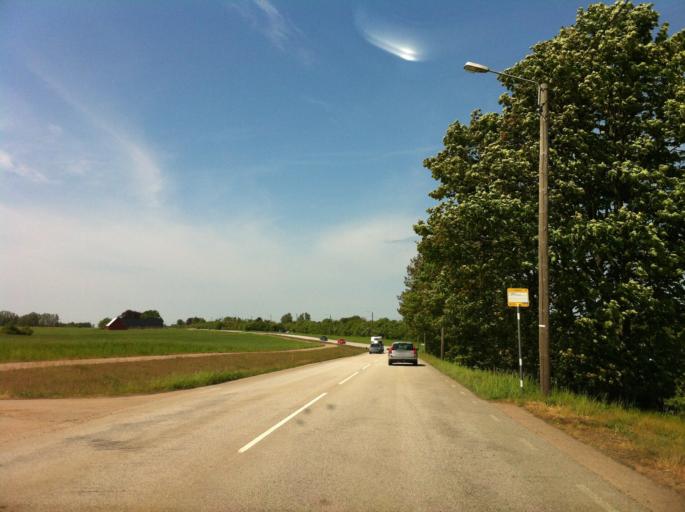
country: SE
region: Skane
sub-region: Helsingborg
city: Glumslov
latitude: 55.9249
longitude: 12.8428
